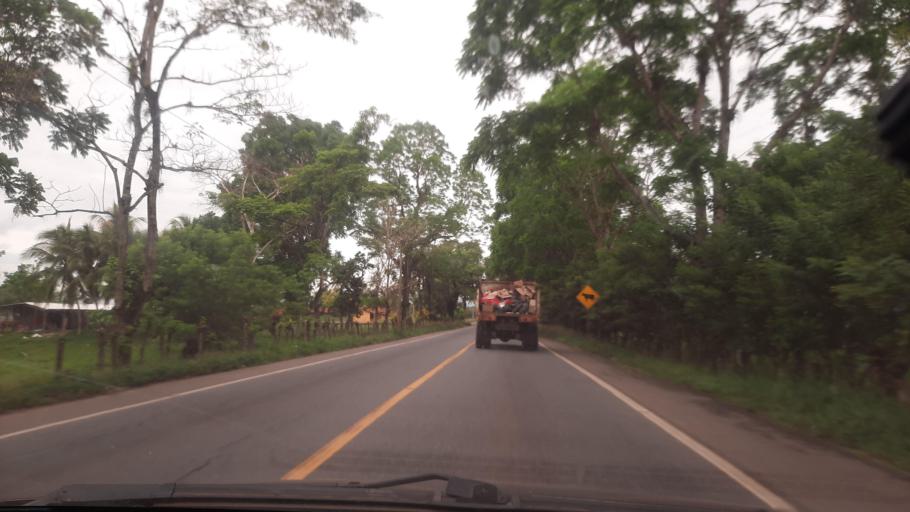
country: GT
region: Izabal
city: Morales
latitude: 15.4715
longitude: -88.9007
